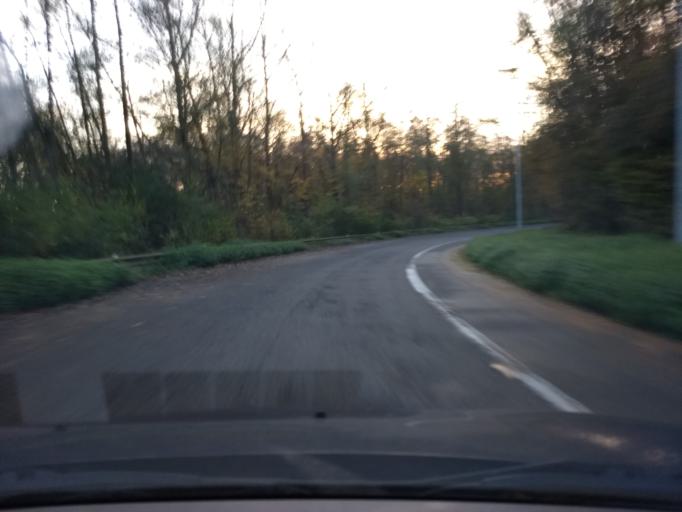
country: BE
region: Wallonia
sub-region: Province du Brabant Wallon
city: Braine-le-Chateau
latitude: 50.6585
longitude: 4.3134
